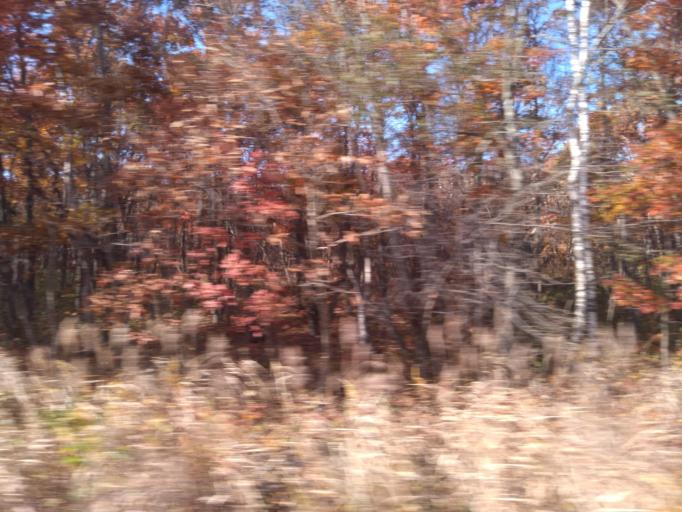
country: JP
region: Hokkaido
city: Tomakomai
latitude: 42.6909
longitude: 141.7290
